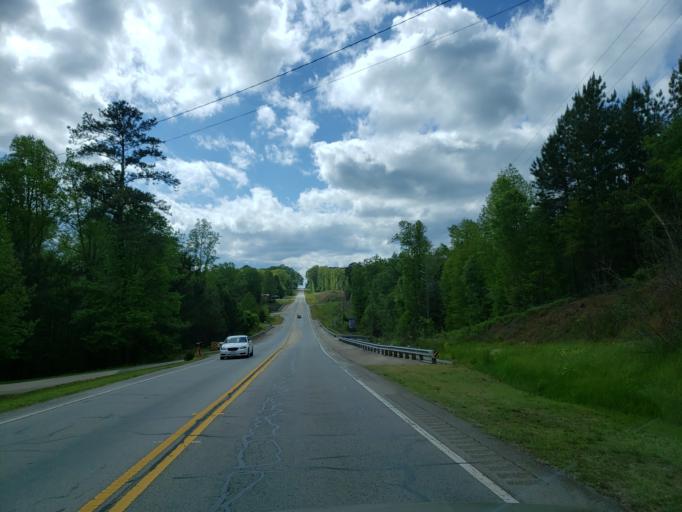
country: US
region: Georgia
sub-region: Haralson County
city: Tallapoosa
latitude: 33.7394
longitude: -85.2689
